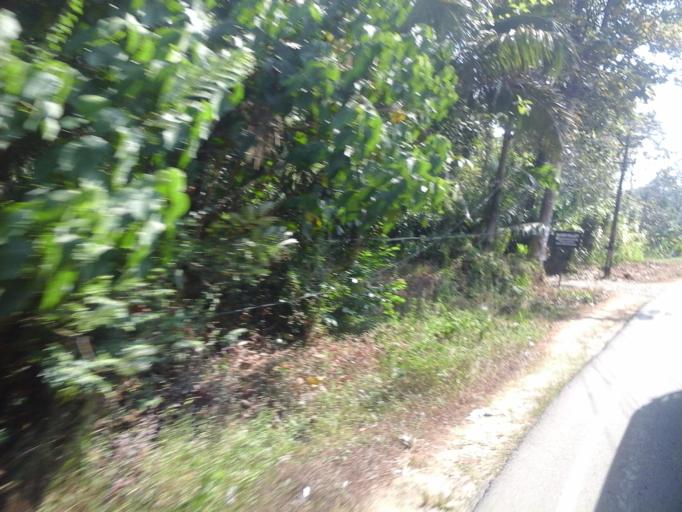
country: IN
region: Kerala
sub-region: Kottayam
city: Erattupetta
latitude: 9.7037
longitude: 76.7476
